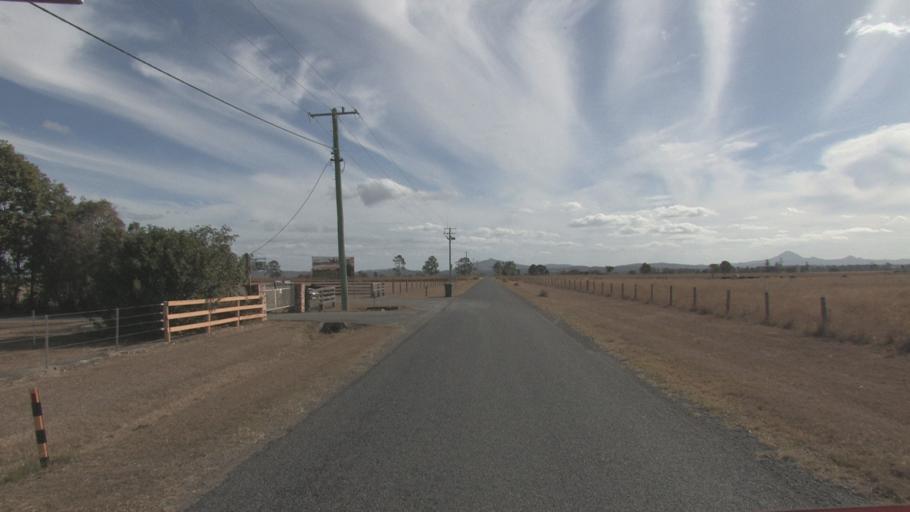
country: AU
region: Queensland
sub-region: Logan
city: Cedar Vale
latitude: -27.9238
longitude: 152.9802
